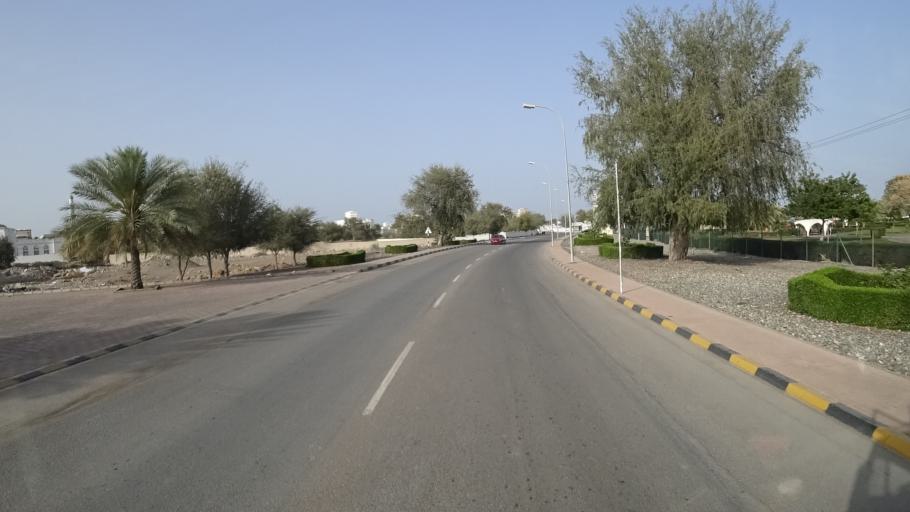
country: OM
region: Muhafazat Masqat
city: Muscat
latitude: 23.2561
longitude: 58.9110
